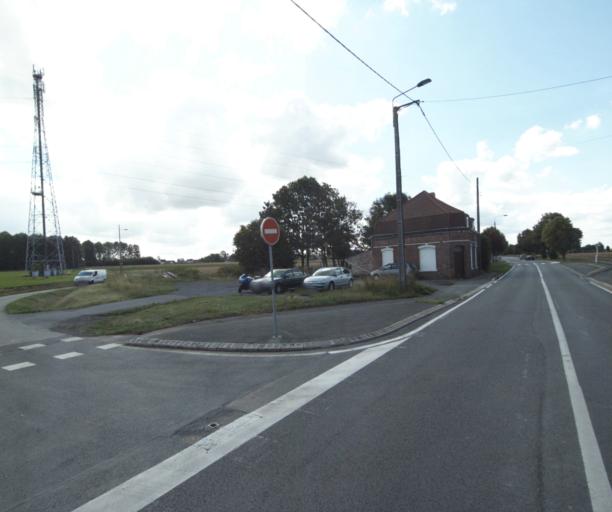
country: FR
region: Nord-Pas-de-Calais
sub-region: Departement du Nord
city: Willems
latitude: 50.6401
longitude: 3.2354
